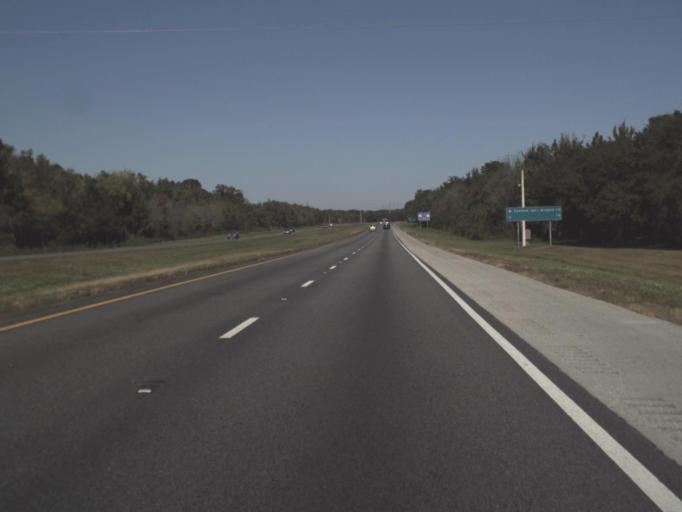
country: US
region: Florida
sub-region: Seminole County
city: Goldenrod
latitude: 28.6334
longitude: -81.2441
